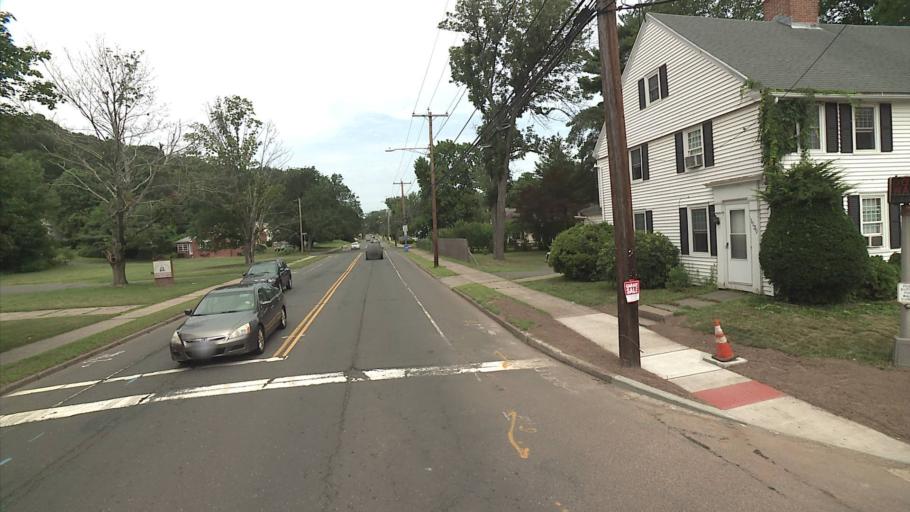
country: US
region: Connecticut
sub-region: Hartford County
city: New Britain
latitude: 41.6984
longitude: -72.7742
